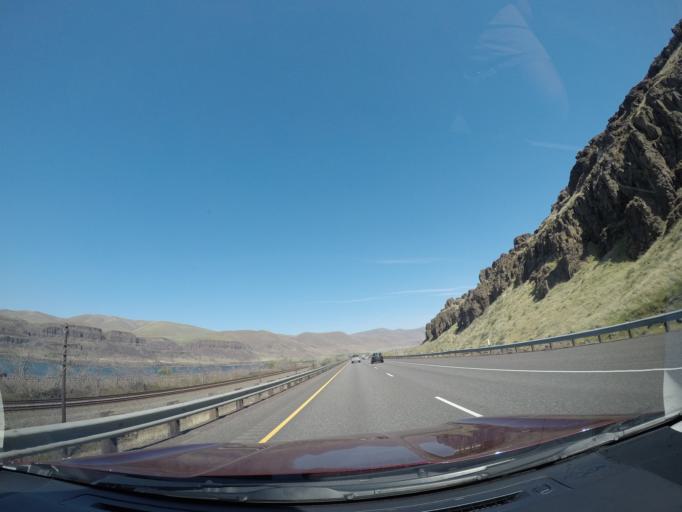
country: US
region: Washington
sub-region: Klickitat County
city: Dallesport
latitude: 45.6441
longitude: -121.0746
